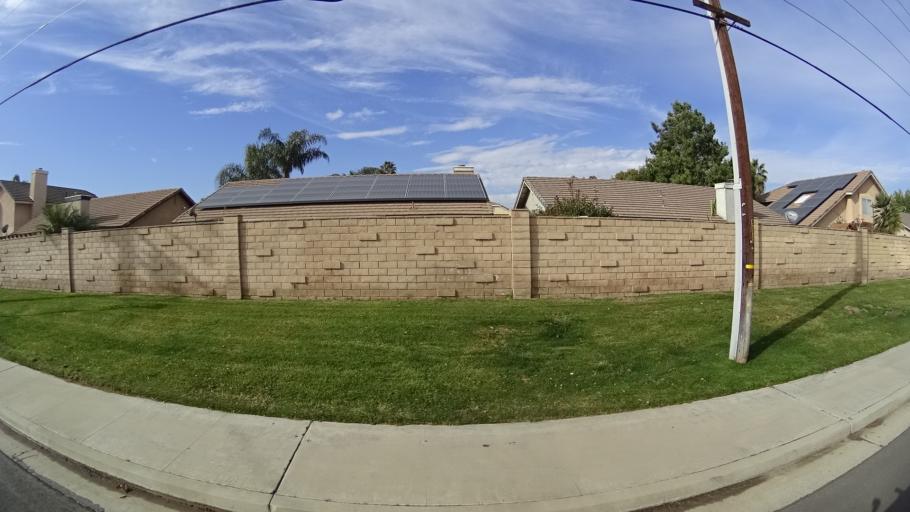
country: US
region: California
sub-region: Kern County
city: Rosedale
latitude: 35.3895
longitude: -119.1279
